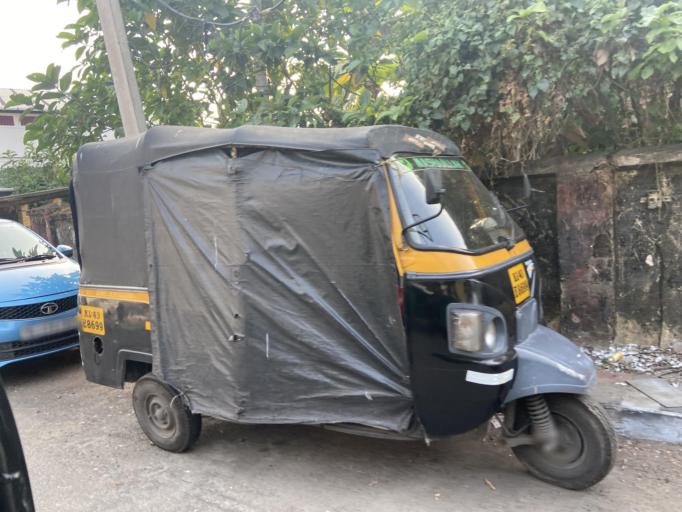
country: IN
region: Kerala
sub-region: Ernakulam
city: Cochin
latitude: 9.9498
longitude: 76.2590
